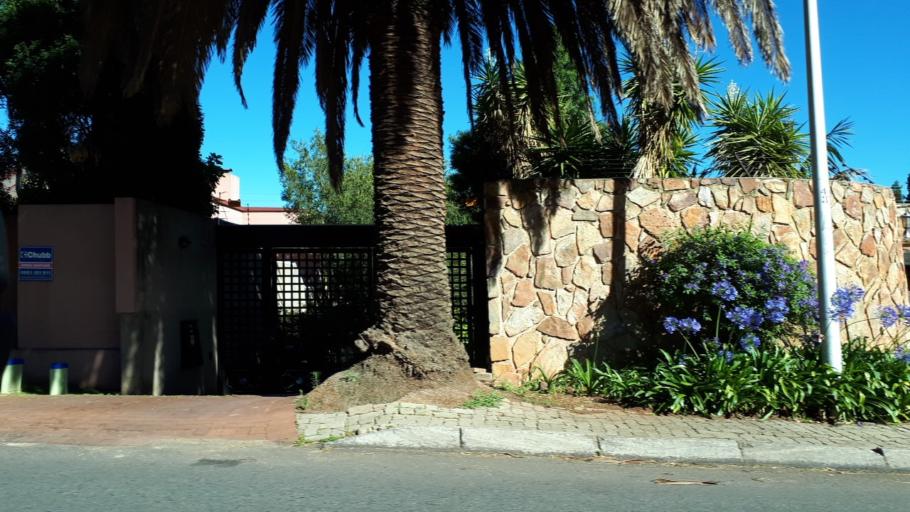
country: ZA
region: Gauteng
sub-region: Ekurhuleni Metropolitan Municipality
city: Germiston
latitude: -26.1837
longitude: 28.1451
